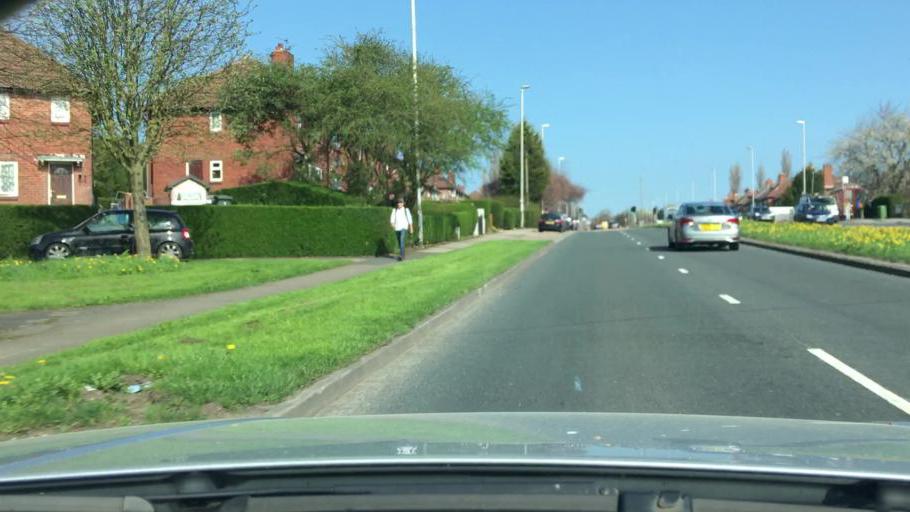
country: GB
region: England
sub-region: City and Borough of Leeds
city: Chapel Allerton
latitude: 53.8177
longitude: -1.5399
